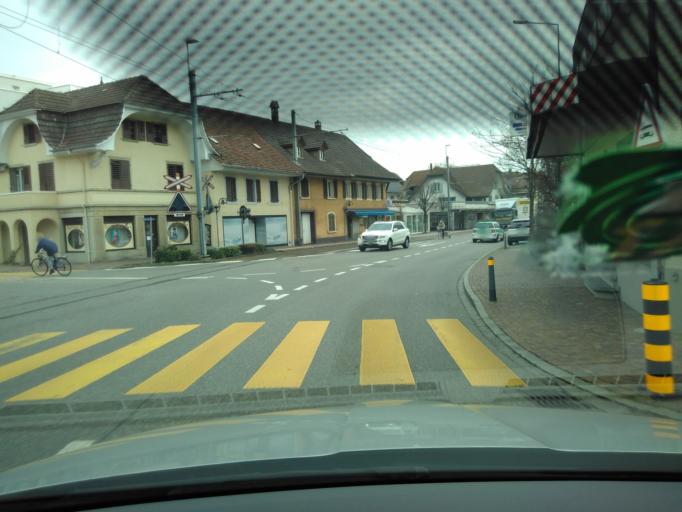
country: CH
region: Aargau
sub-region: Bezirk Aarau
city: Oberentfelden
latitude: 47.3555
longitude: 8.0467
